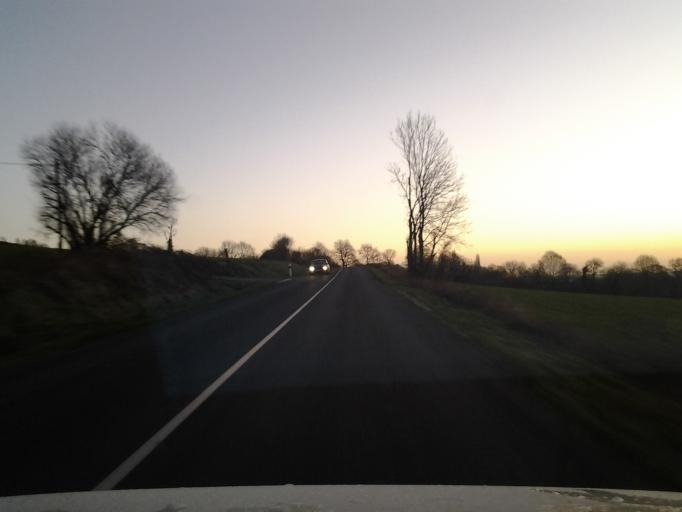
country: FR
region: Pays de la Loire
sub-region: Departement de la Vendee
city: Les Epesses
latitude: 46.8788
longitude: -0.9189
